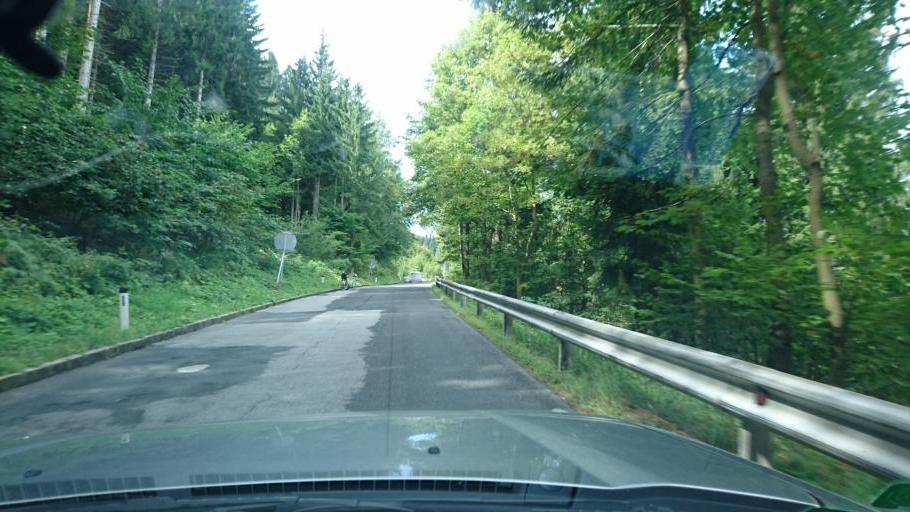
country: AT
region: Carinthia
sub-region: Politischer Bezirk Villach Land
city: Arnoldstein
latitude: 46.5370
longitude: 13.7514
